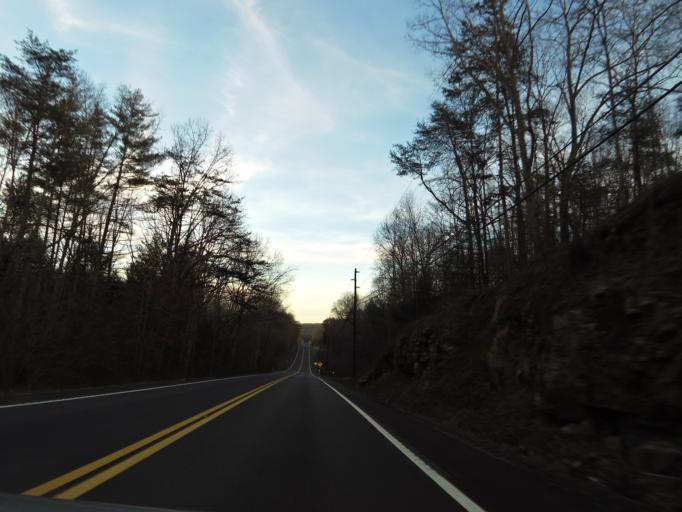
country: US
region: Tennessee
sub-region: Roane County
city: Rockwood
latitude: 35.8605
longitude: -84.7504
